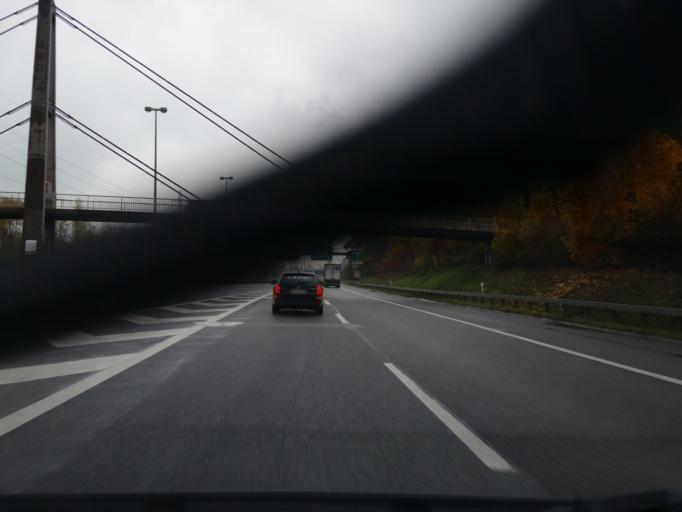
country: CH
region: Zurich
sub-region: Bezirk Zuerich
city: Zuerich (Kreis 12) / Hirzenbach
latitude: 47.4085
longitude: 8.5885
